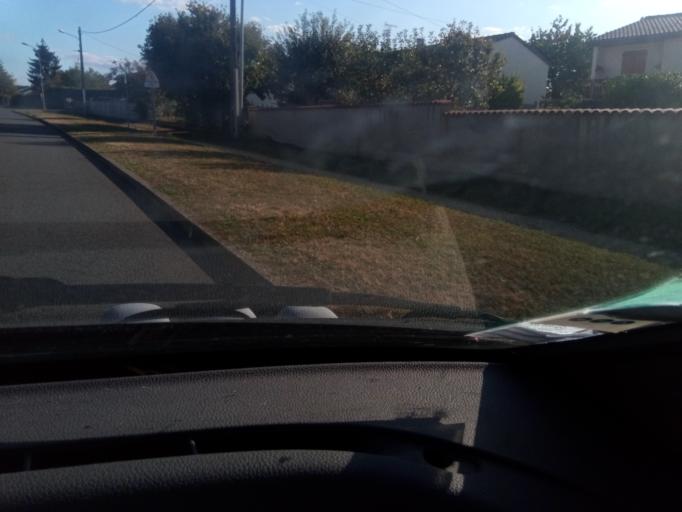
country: FR
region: Poitou-Charentes
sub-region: Departement de la Vienne
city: Lussac-les-Chateaux
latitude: 46.4024
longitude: 0.7153
